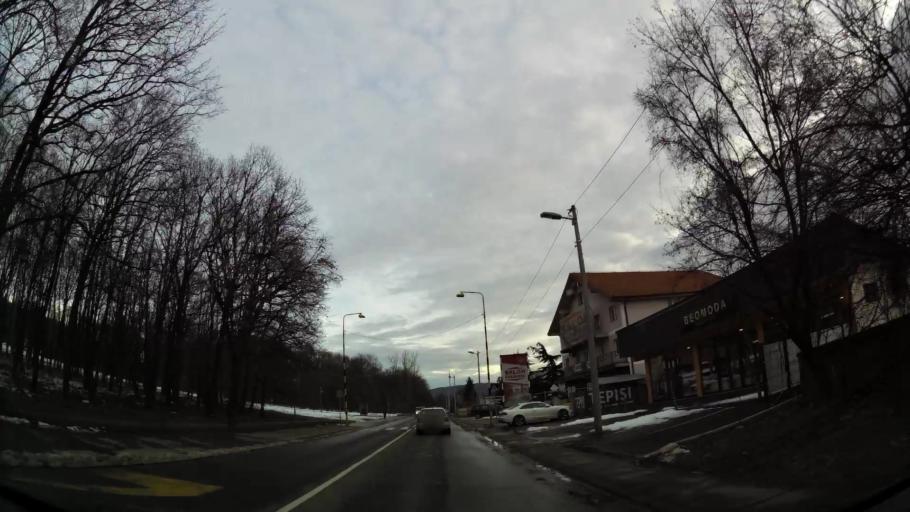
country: RS
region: Central Serbia
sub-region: Belgrade
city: Rakovica
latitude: 44.7294
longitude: 20.4843
